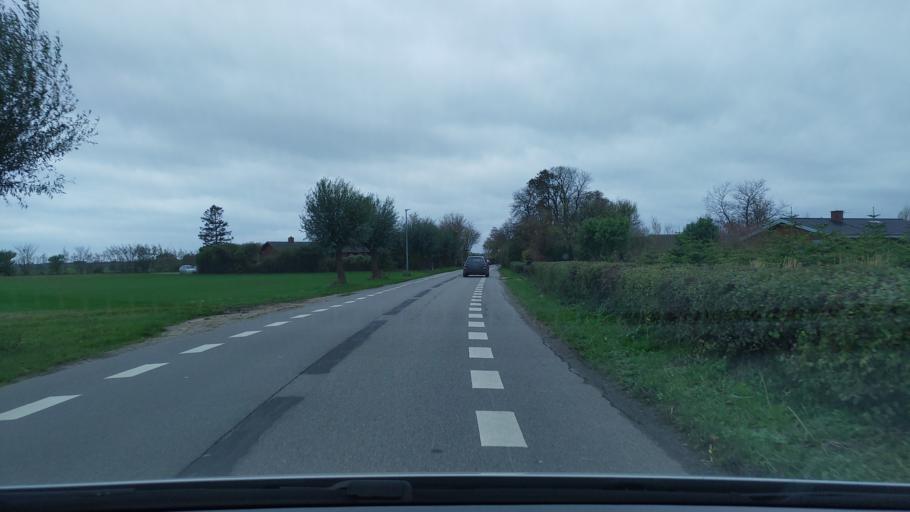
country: DK
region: Capital Region
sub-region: Tarnby Kommune
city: Tarnby
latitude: 55.5975
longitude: 12.6014
